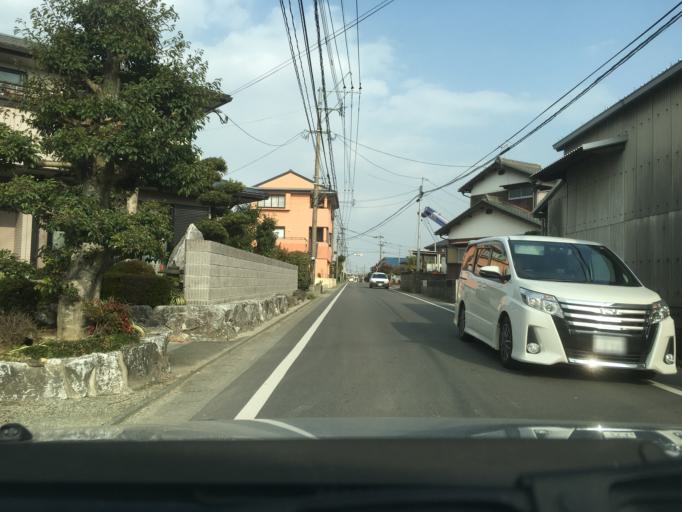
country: JP
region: Fukuoka
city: Kurume
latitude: 33.2706
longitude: 130.4922
